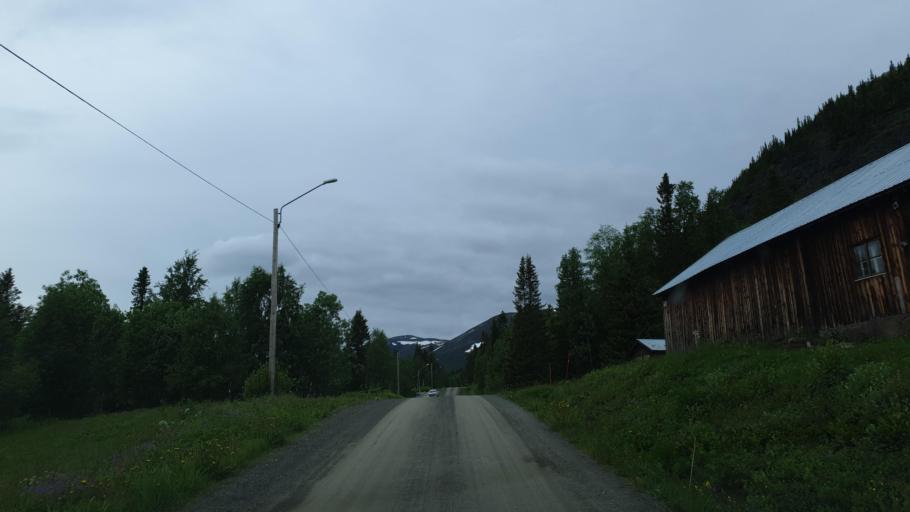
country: SE
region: Vaesterbotten
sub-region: Vilhelmina Kommun
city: Sjoberg
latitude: 65.3478
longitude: 15.8578
